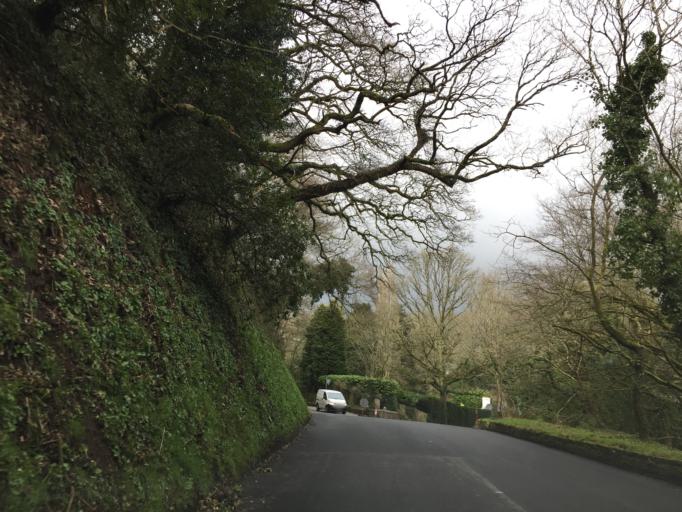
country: JE
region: St Helier
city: Saint Helier
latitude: 49.2190
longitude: -2.1743
